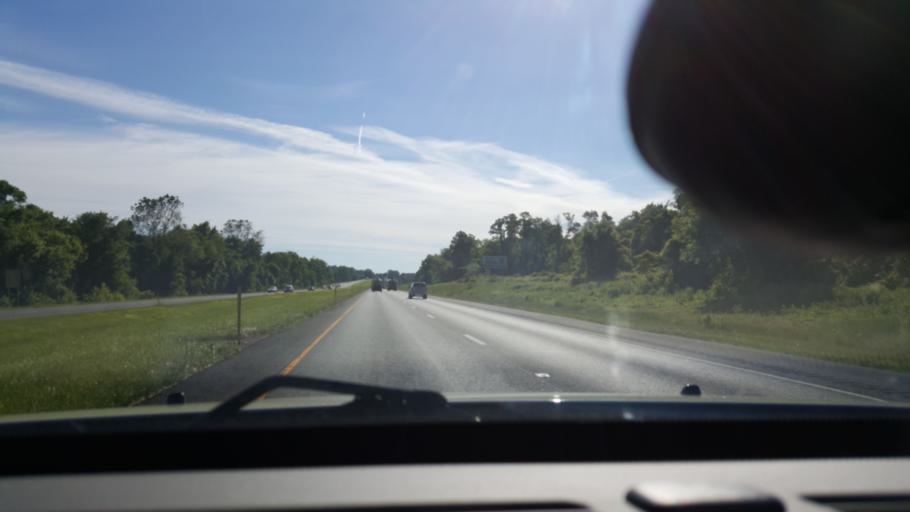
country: US
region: Pennsylvania
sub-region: York County
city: Yorklyn
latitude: 40.0025
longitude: -76.6279
